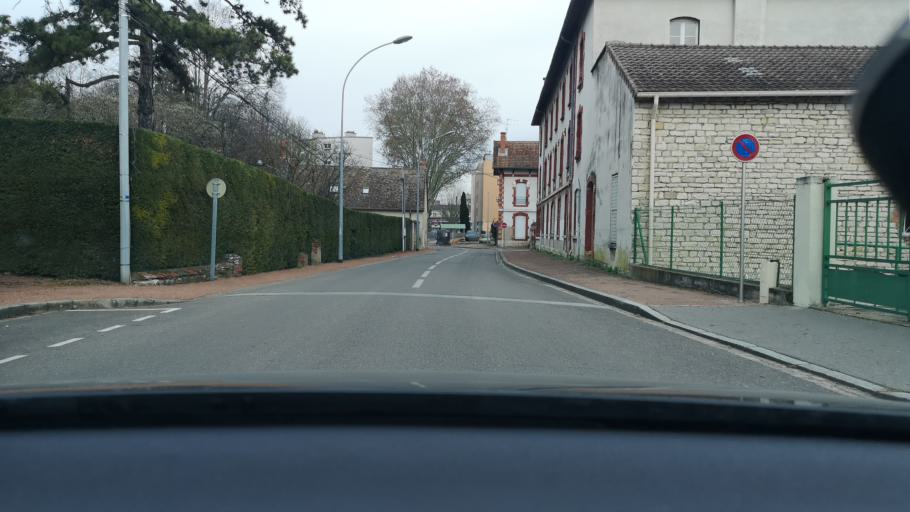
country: FR
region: Bourgogne
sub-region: Departement de Saone-et-Loire
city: Chalon-sur-Saone
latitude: 46.7798
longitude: 4.8405
